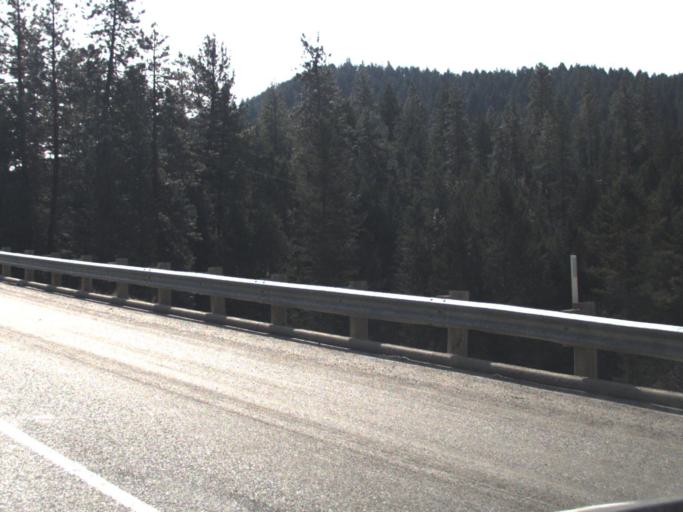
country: US
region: Washington
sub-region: Stevens County
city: Colville
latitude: 48.5435
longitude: -117.8504
